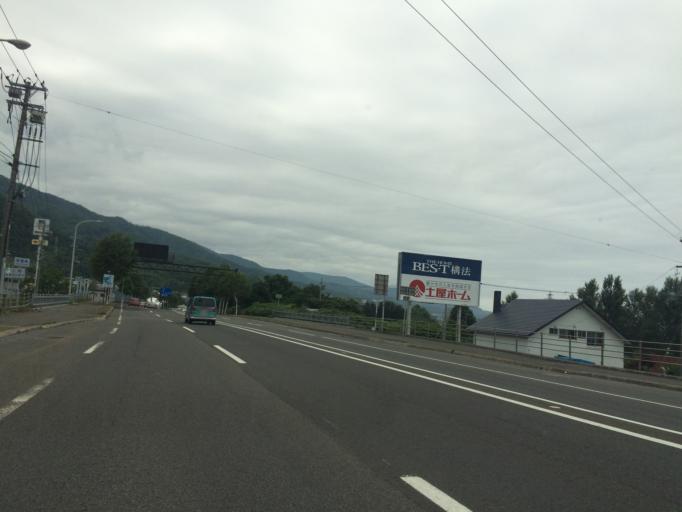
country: JP
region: Hokkaido
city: Sapporo
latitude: 43.1317
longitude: 141.1951
